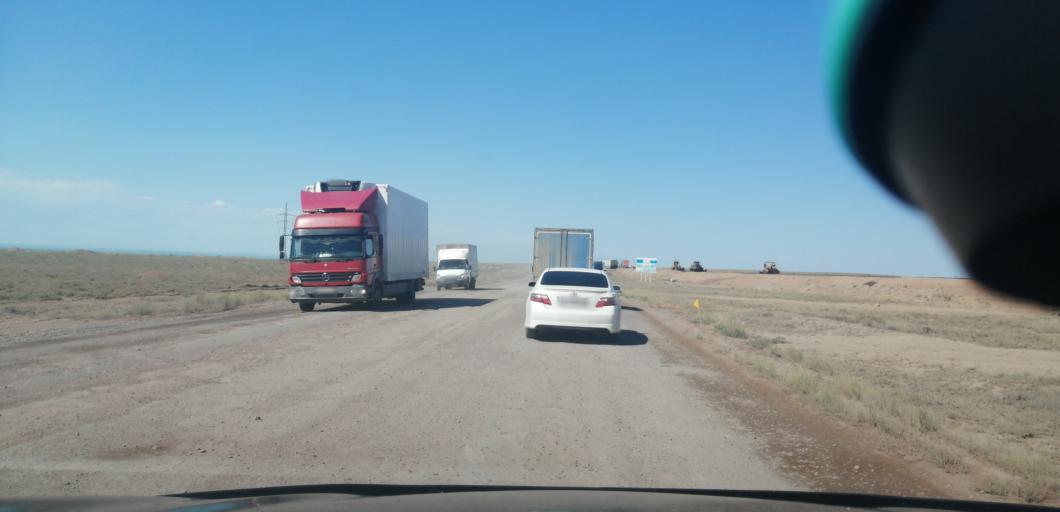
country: KZ
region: Qaraghandy
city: Balqash
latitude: 46.8226
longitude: 74.7723
